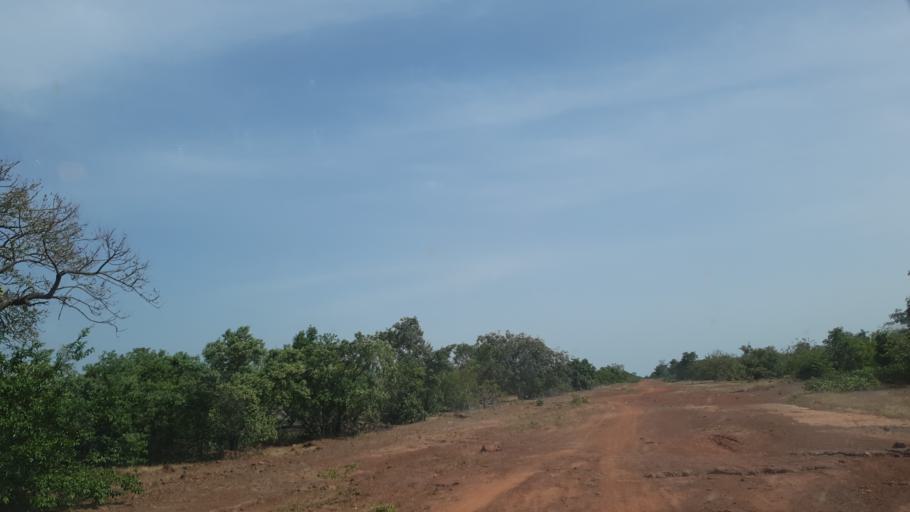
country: ML
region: Koulikoro
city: Dioila
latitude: 12.4405
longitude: -6.2081
